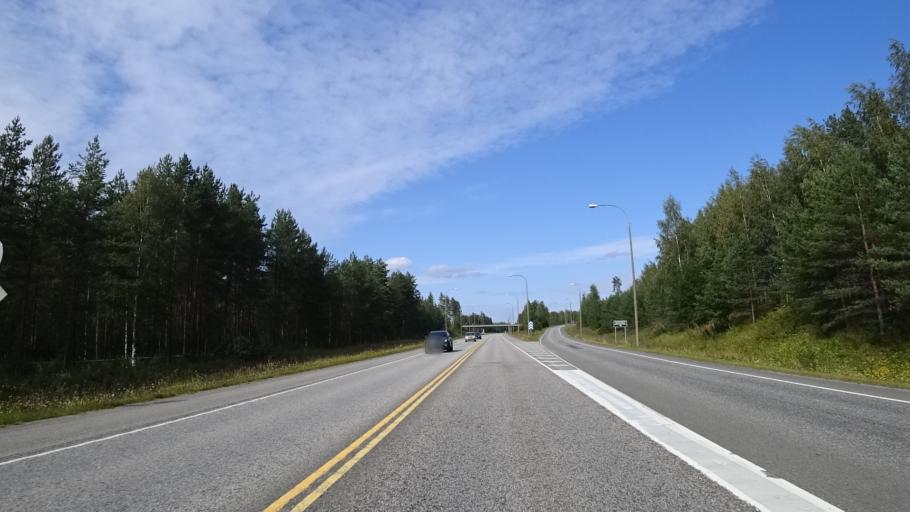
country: FI
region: North Karelia
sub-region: Joensuu
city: Joensuu
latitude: 62.6697
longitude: 29.7894
